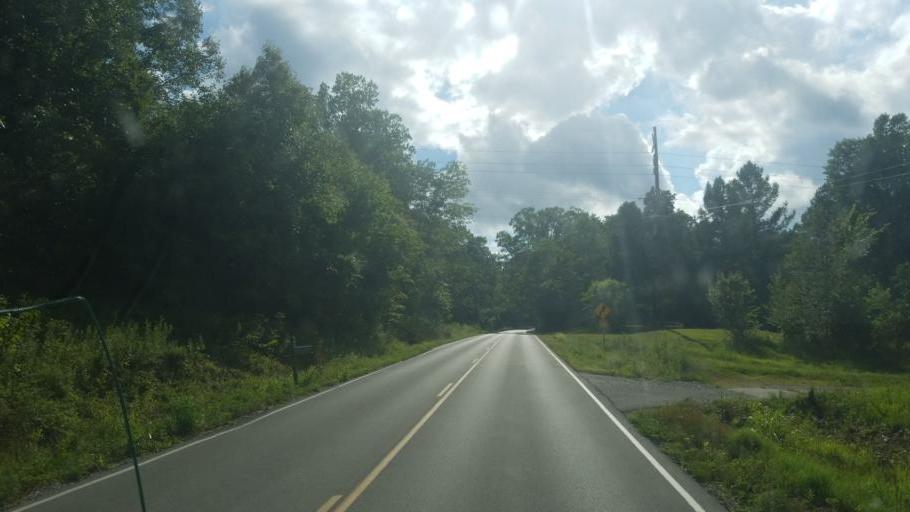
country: US
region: Illinois
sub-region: Union County
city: Cobden
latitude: 37.5445
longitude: -89.2690
